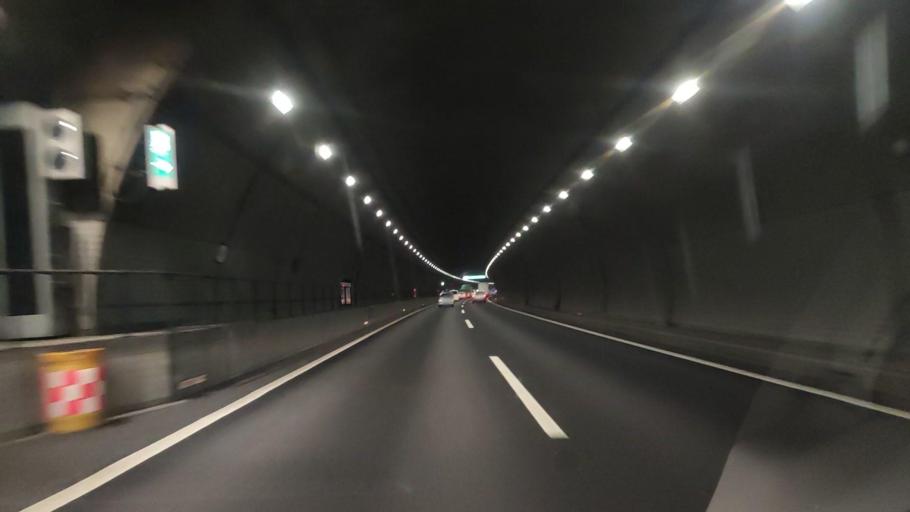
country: JP
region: Kanagawa
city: Zama
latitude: 35.5275
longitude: 139.3457
